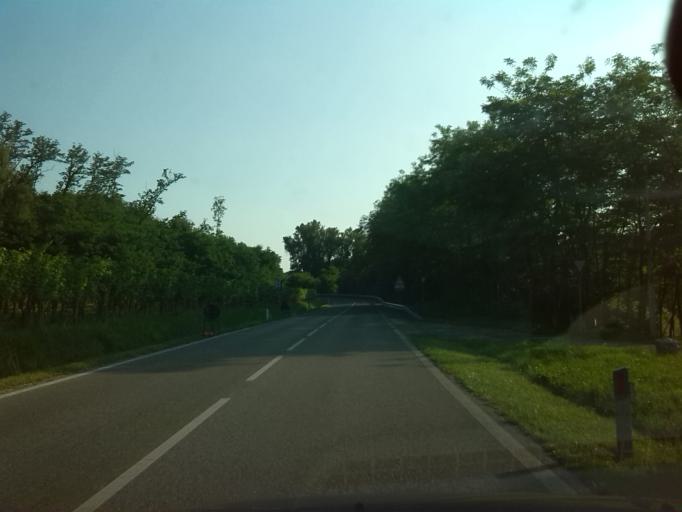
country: IT
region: Friuli Venezia Giulia
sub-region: Provincia di Gorizia
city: Dolegna del Collio
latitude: 46.0140
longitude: 13.4737
